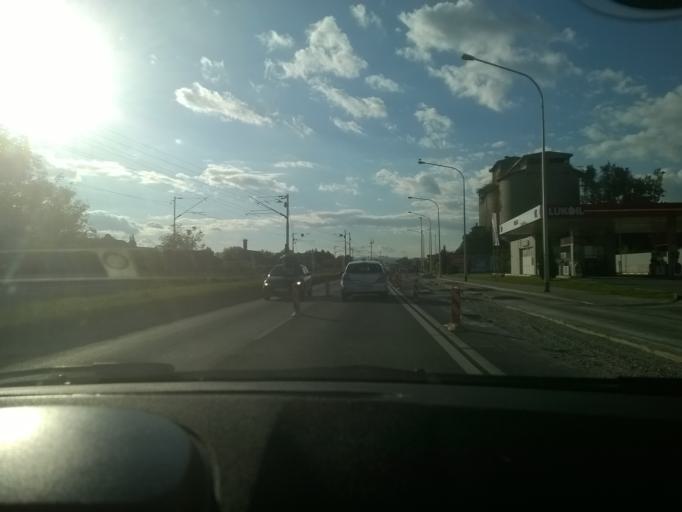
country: HR
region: Grad Zagreb
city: Stenjevec
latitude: 45.8148
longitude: 15.8532
